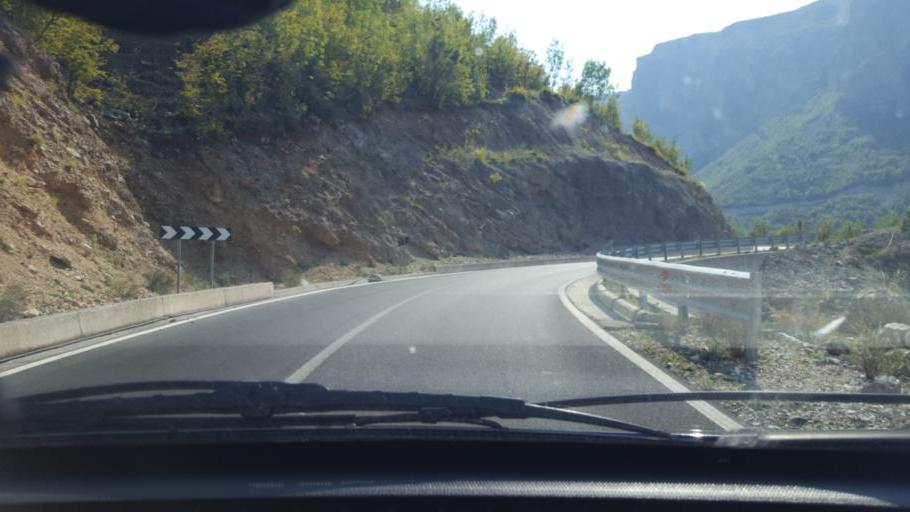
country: AL
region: Shkoder
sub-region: Rrethi i Malesia e Madhe
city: Kastrat
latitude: 42.4209
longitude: 19.5108
